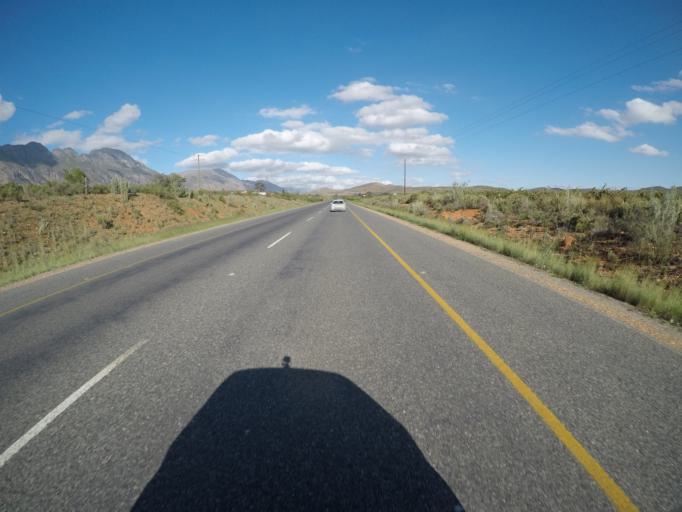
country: ZA
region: Western Cape
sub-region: Cape Winelands District Municipality
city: Ashton
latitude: -33.8539
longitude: 20.1044
